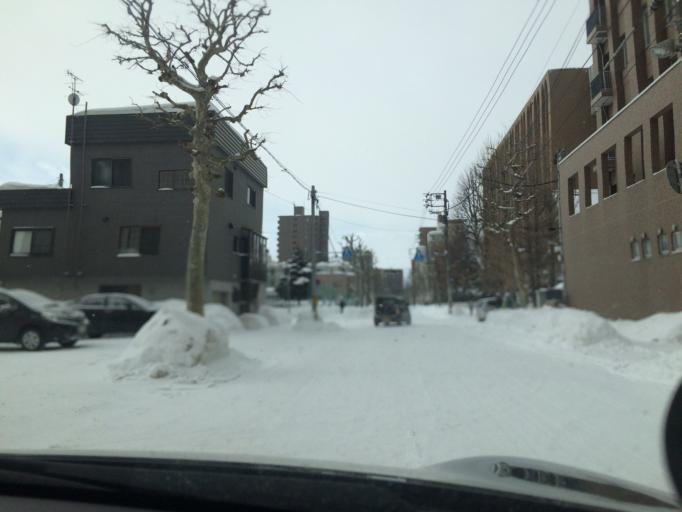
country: JP
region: Hokkaido
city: Sapporo
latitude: 43.0798
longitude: 141.3510
